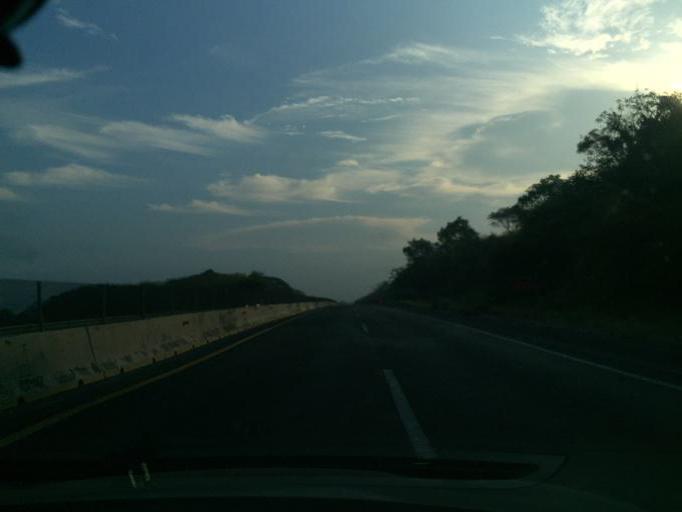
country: MX
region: Veracruz
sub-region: Tierra Blanca
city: Huixcolotla
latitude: 18.7854
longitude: -96.5113
